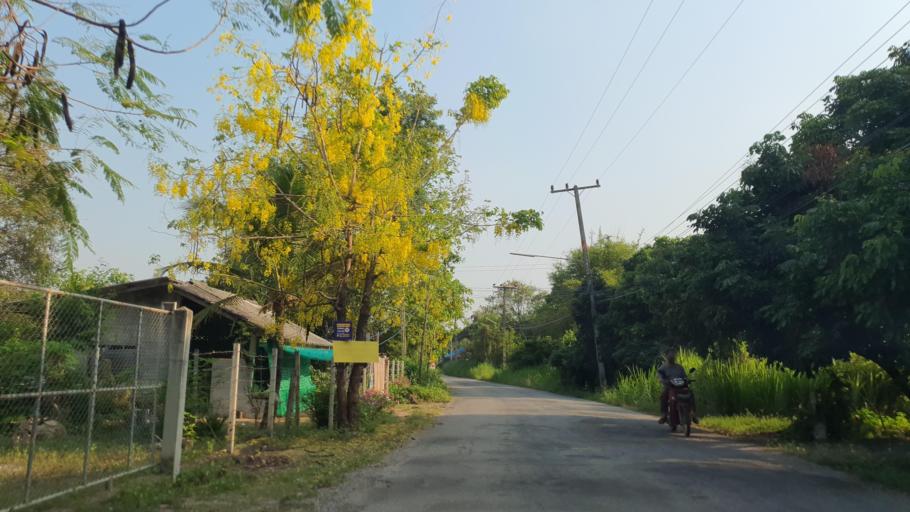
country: TH
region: Chiang Mai
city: Mae Wang
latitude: 18.6196
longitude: 98.8204
